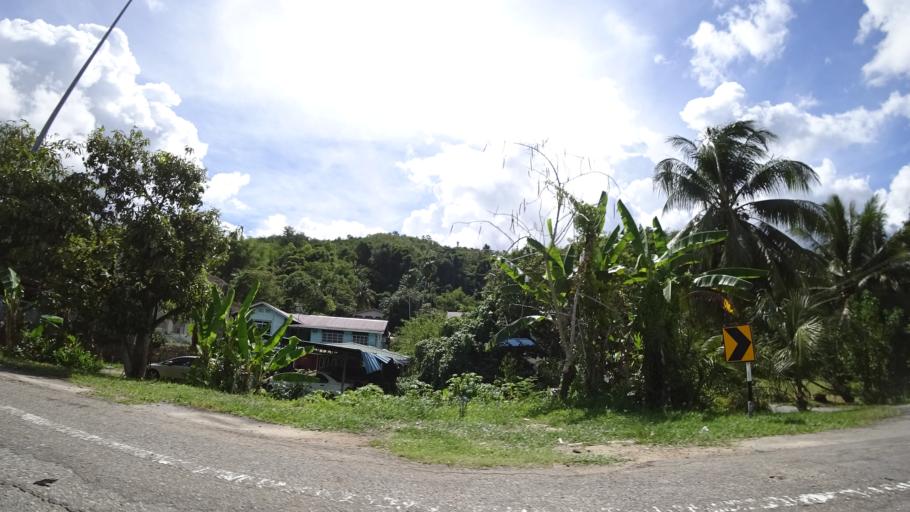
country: BN
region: Brunei and Muara
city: Bandar Seri Begawan
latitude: 4.8878
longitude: 114.9735
